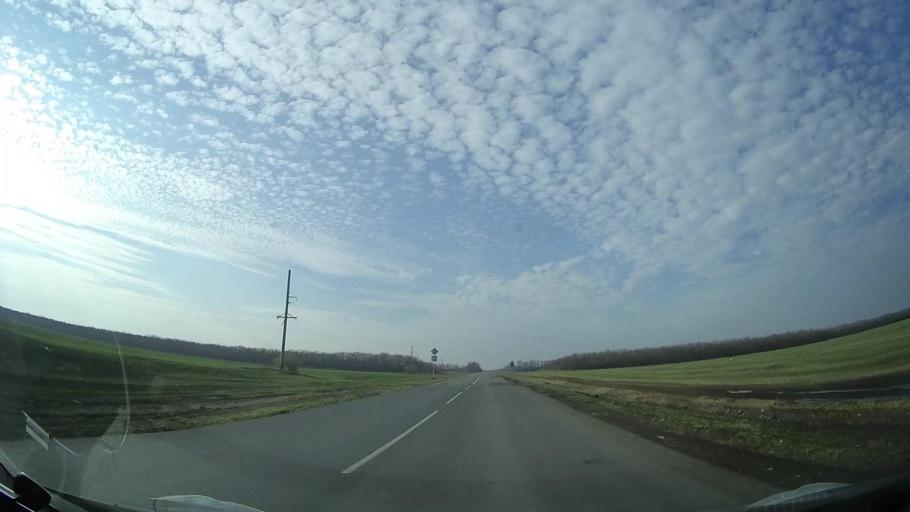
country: RU
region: Rostov
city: Veselyy
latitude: 46.9711
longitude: 40.7138
